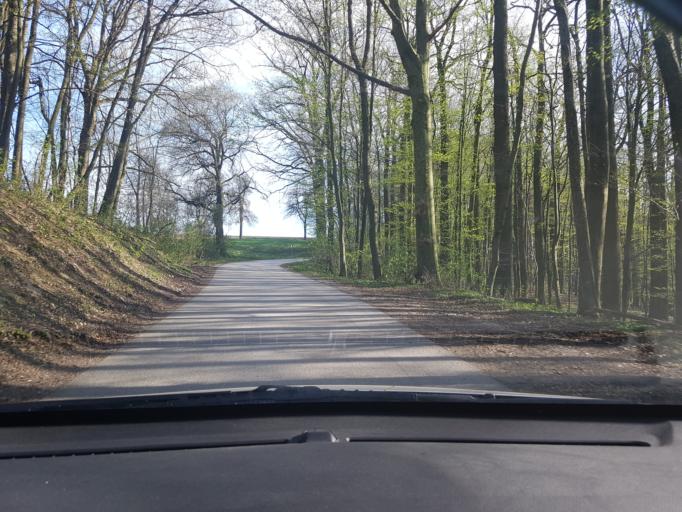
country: AT
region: Upper Austria
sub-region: Politischer Bezirk Linz-Land
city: Ansfelden
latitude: 48.1752
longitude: 14.3298
